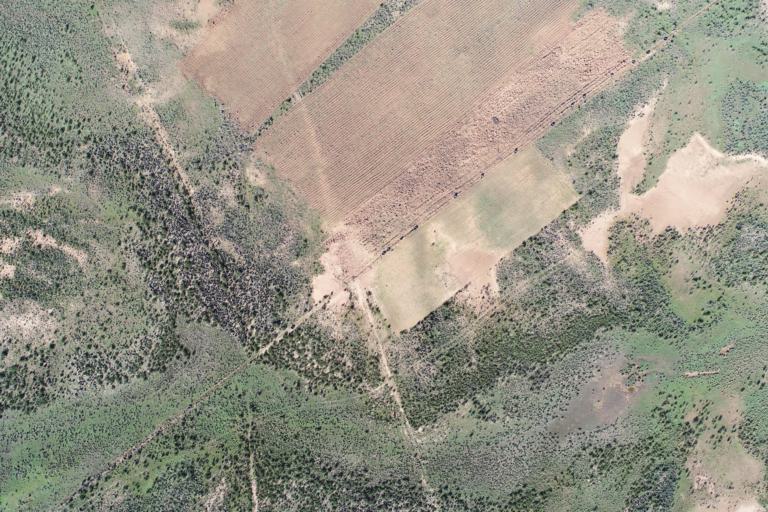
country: BO
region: La Paz
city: Curahuara de Carangas
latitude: -17.3017
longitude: -68.5007
